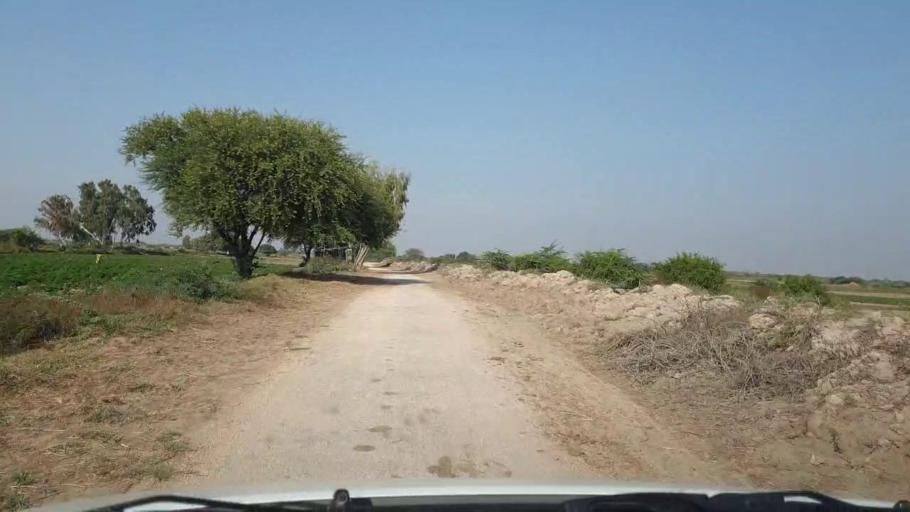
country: PK
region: Sindh
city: Mirpur Sakro
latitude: 24.5953
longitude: 67.6297
